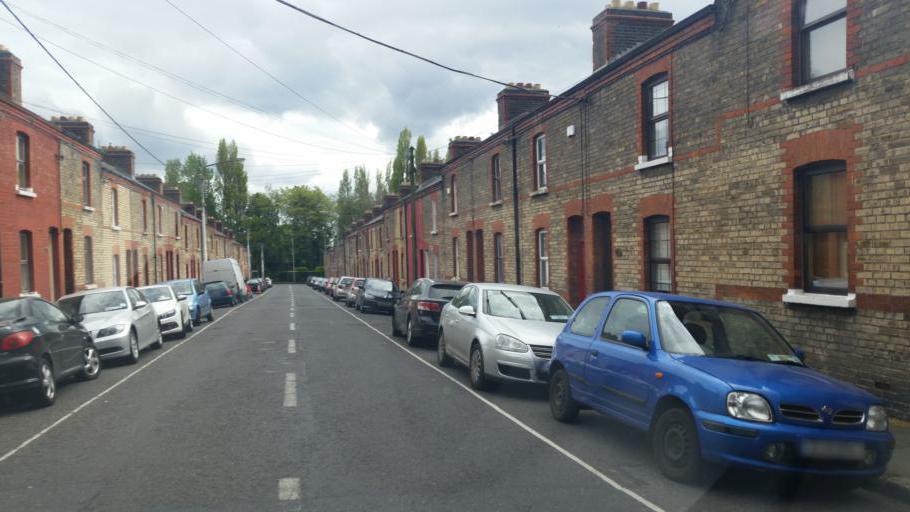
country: IE
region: Leinster
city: Cabra
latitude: 53.3522
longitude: -6.2888
